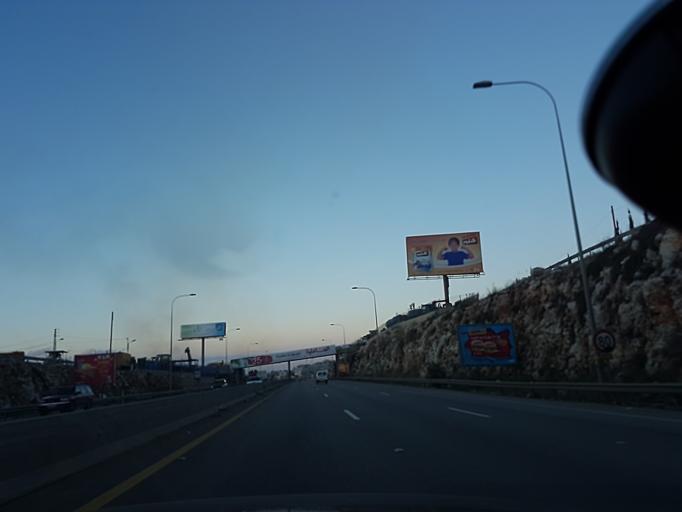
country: LB
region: Liban-Sud
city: Sidon
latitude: 33.6316
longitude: 35.4022
